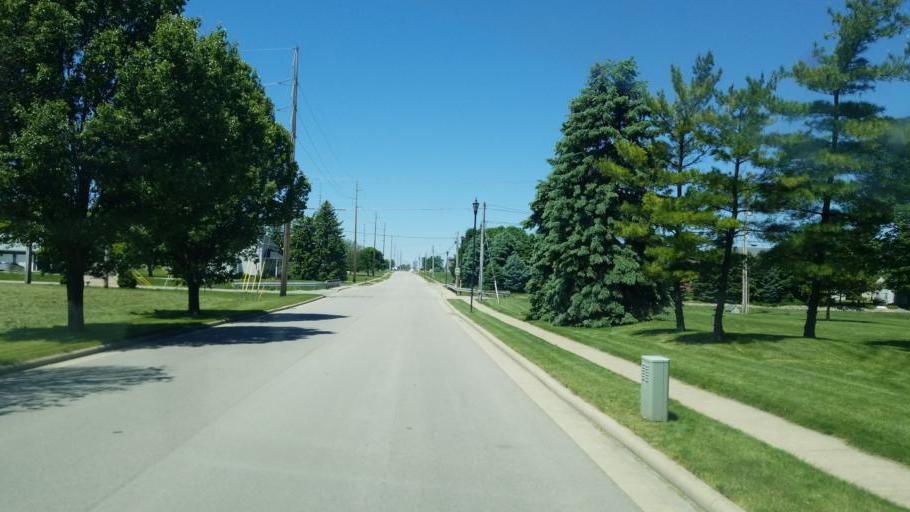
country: US
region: Ohio
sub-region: Auglaize County
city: Minster
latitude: 40.3858
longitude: -84.3825
